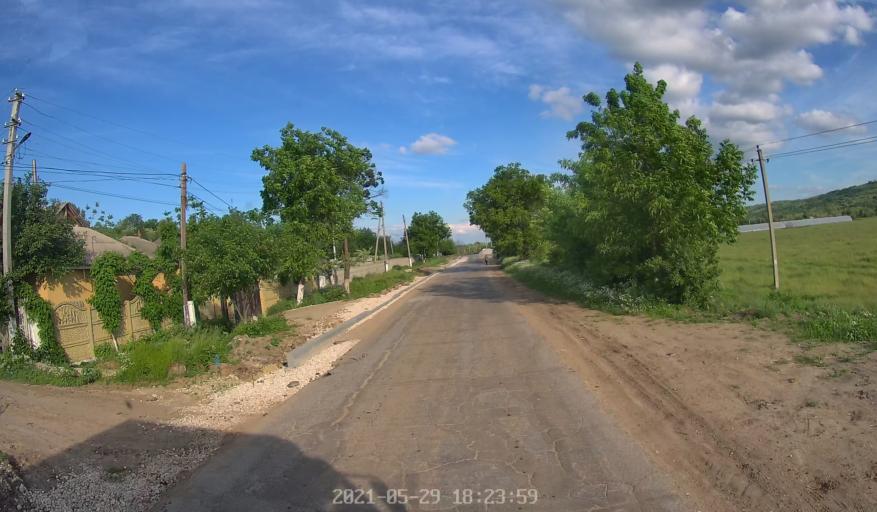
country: MD
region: Chisinau
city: Singera
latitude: 46.8312
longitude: 28.8599
